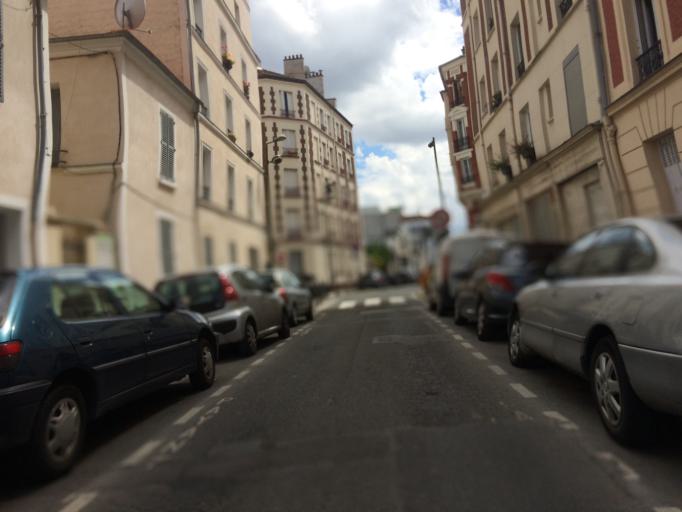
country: FR
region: Ile-de-France
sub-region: Departement des Hauts-de-Seine
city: Puteaux
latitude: 48.8786
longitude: 2.2386
